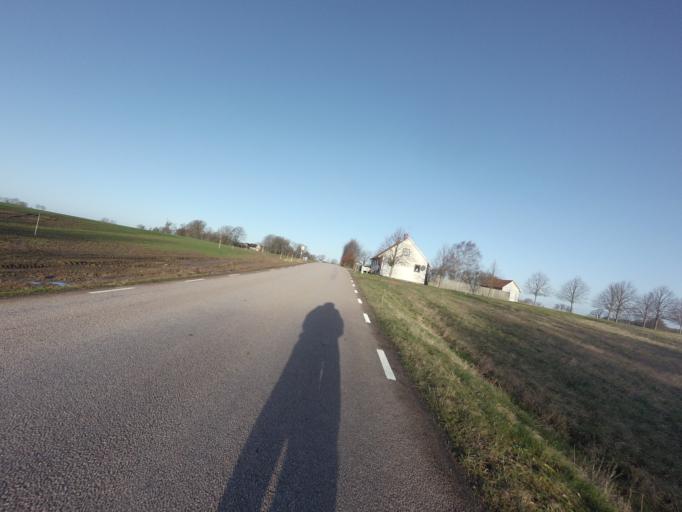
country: SE
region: Skane
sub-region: Helsingborg
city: Odakra
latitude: 56.1168
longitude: 12.6793
